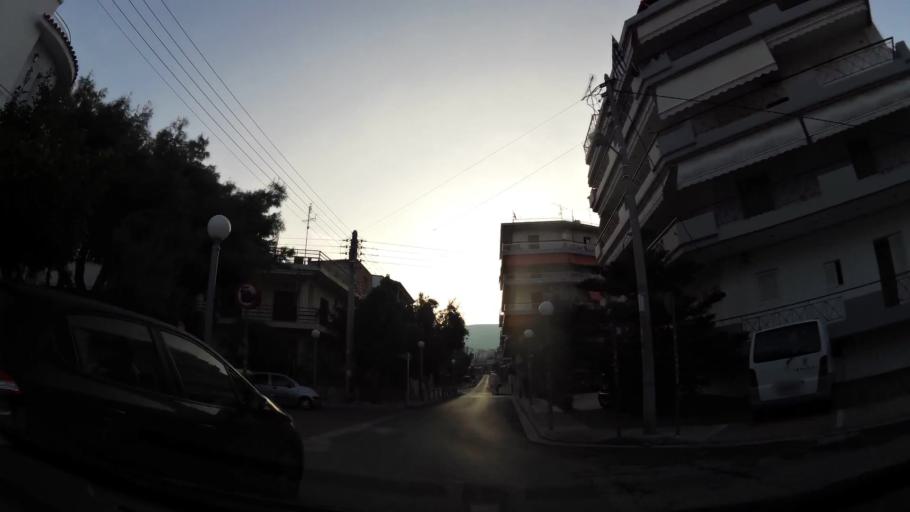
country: GR
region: Attica
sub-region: Nomarchia Athinas
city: Dhafni
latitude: 37.9471
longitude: 23.7426
